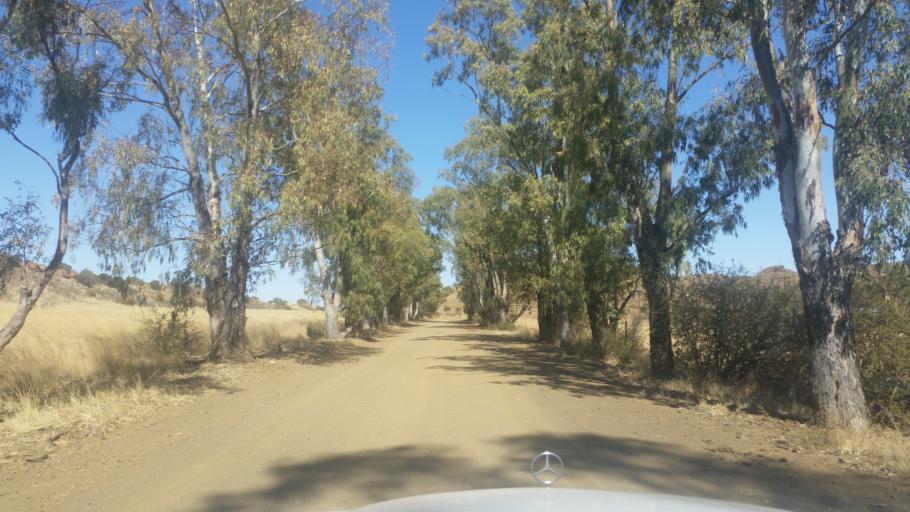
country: ZA
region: Orange Free State
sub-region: Xhariep District Municipality
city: Trompsburg
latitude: -30.4849
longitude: 25.9978
